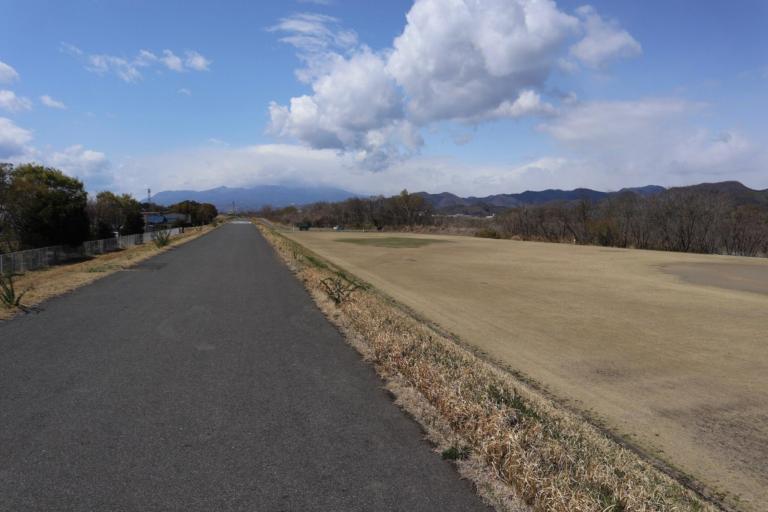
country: JP
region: Gunma
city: Kiryu
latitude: 36.3648
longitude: 139.3686
